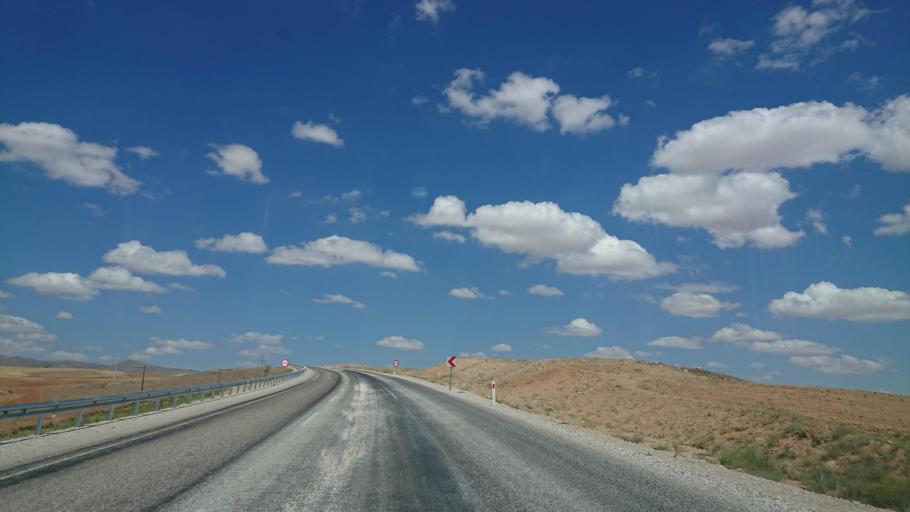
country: TR
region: Ankara
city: Evren
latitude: 39.1072
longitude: 33.9225
